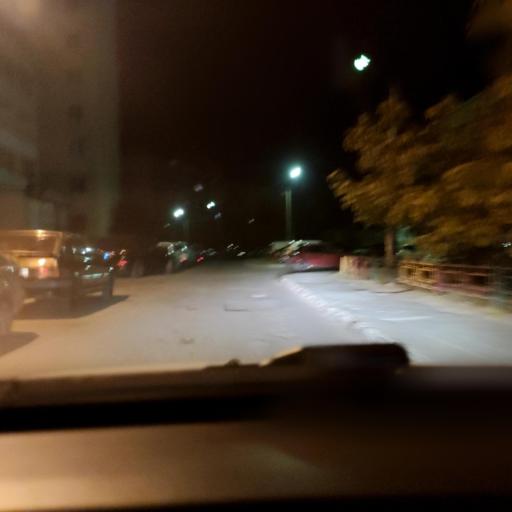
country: RU
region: Voronezj
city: Podgornoye
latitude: 51.7291
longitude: 39.2044
